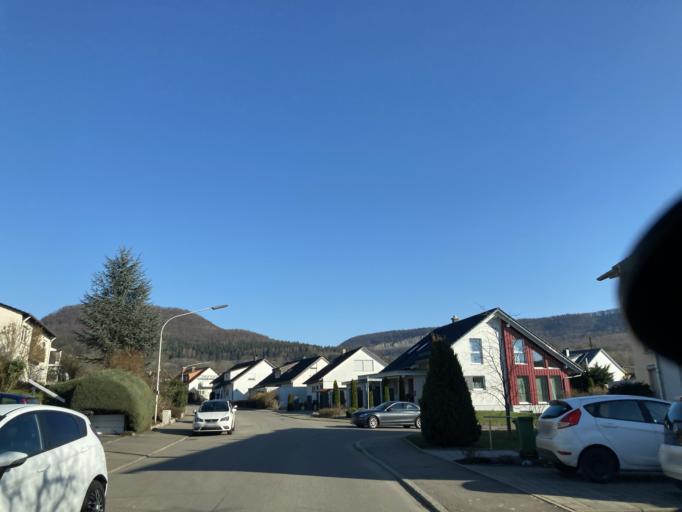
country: DE
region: Baden-Wuerttemberg
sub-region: Tuebingen Region
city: Mossingen
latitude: 48.3944
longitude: 9.0438
